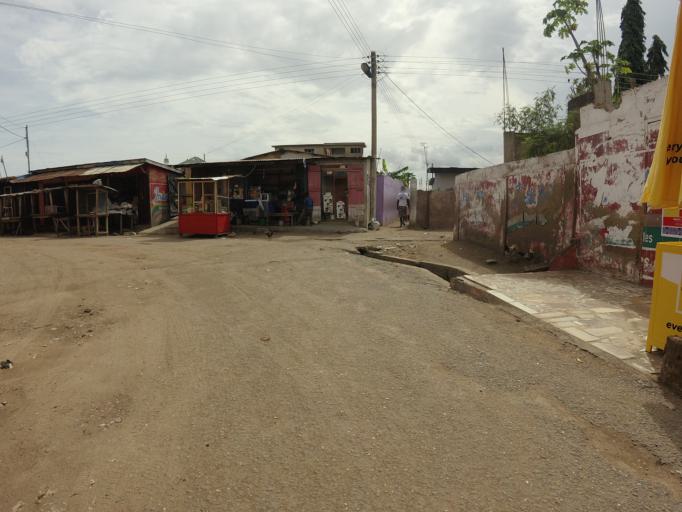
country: GH
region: Greater Accra
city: Accra
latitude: 5.5957
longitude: -0.2136
